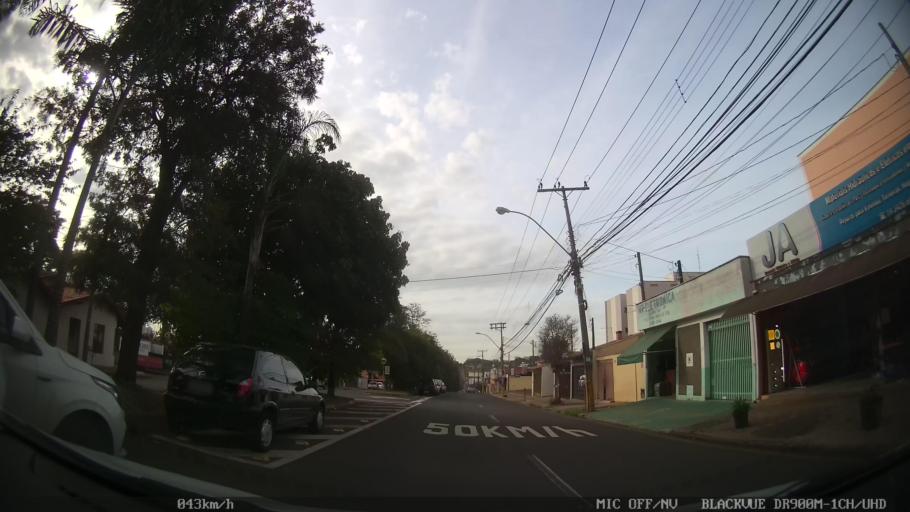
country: BR
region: Sao Paulo
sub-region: Piracicaba
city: Piracicaba
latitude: -22.7358
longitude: -47.6232
